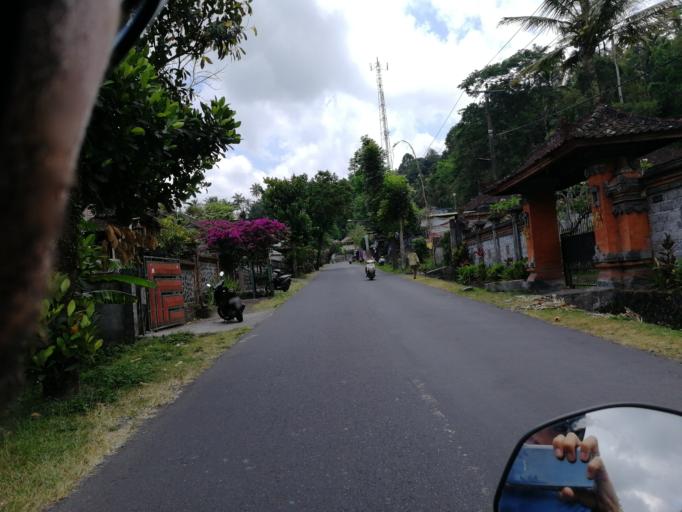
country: ID
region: Bali
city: Banjar Wangsian
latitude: -8.4562
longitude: 115.4514
